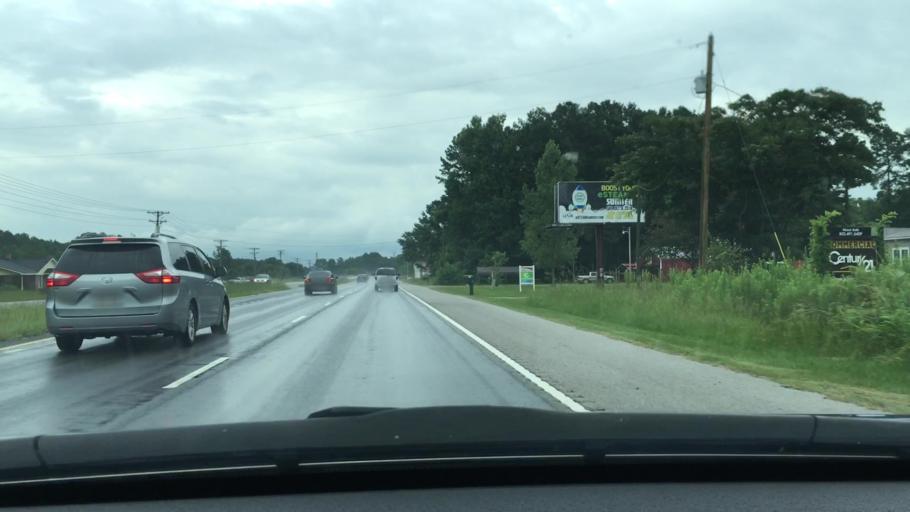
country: US
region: South Carolina
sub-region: Sumter County
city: Cherryvale
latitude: 33.9639
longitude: -80.4359
